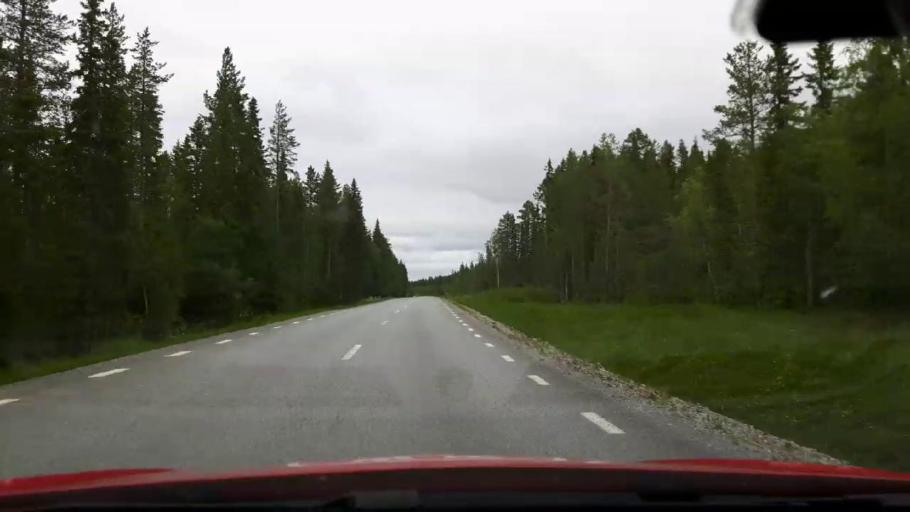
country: SE
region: Jaemtland
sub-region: OEstersunds Kommun
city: Lit
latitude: 63.7033
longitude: 14.6882
